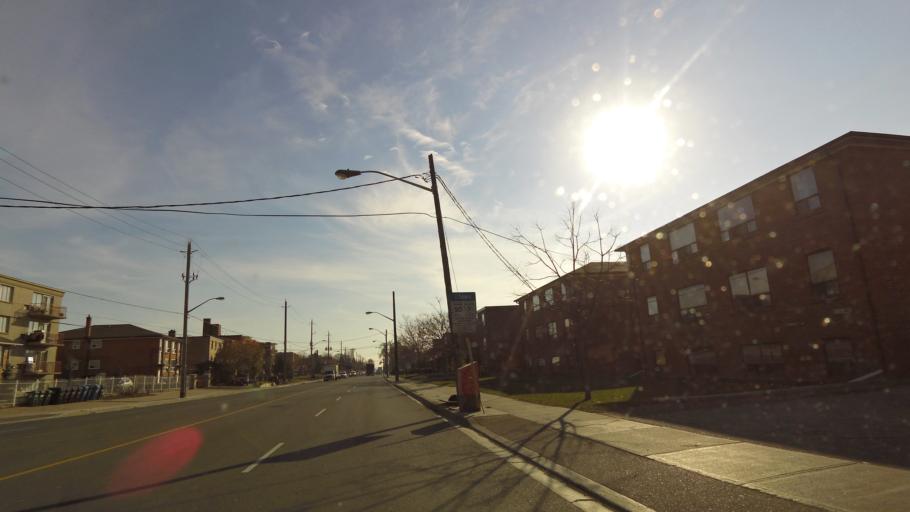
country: CA
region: Ontario
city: Toronto
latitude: 43.7201
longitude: -79.4807
